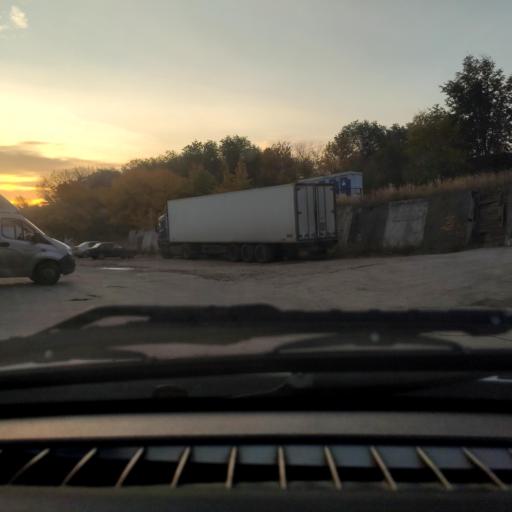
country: RU
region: Samara
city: Zhigulevsk
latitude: 53.4844
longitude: 49.4950
